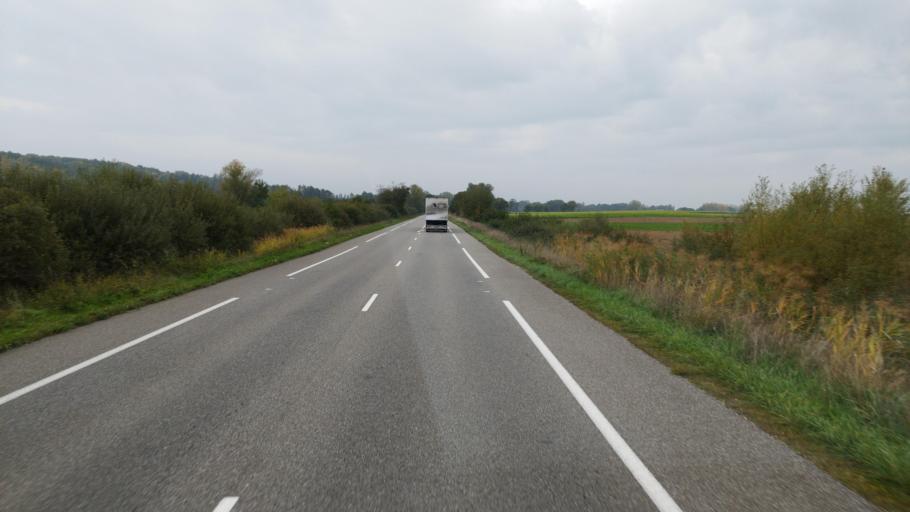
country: FR
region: Alsace
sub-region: Departement du Bas-Rhin
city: Betschdorf
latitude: 48.9424
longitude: 7.9509
